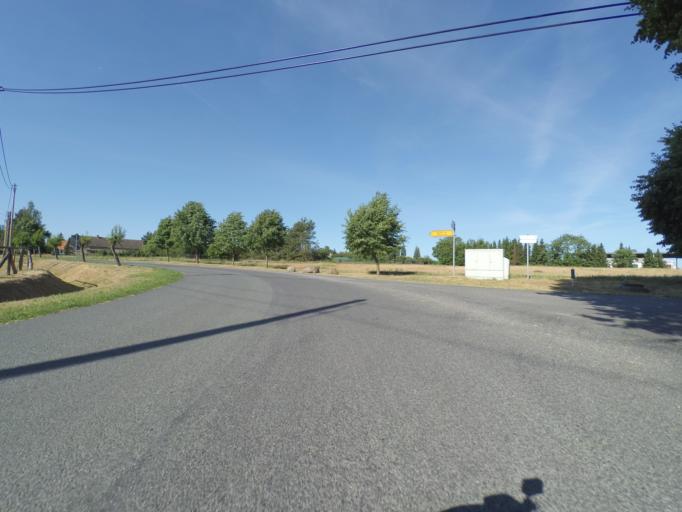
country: DE
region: Mecklenburg-Vorpommern
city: Lubz
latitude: 53.3691
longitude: 12.1007
